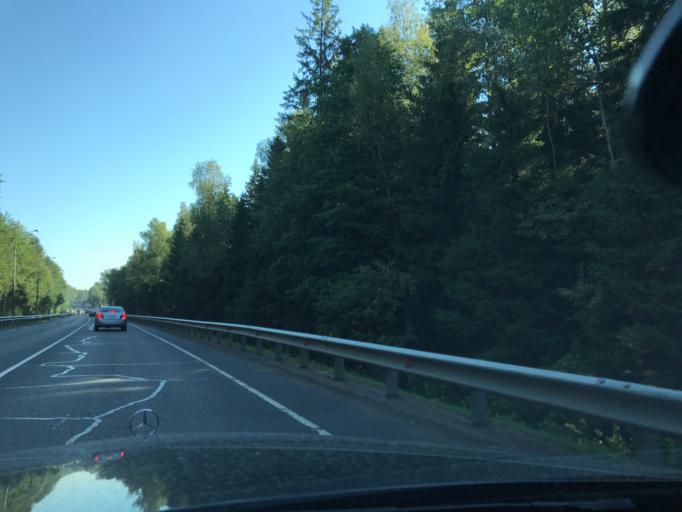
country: RU
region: Moskovskaya
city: Losino-Petrovskiy
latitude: 55.9320
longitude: 38.2100
